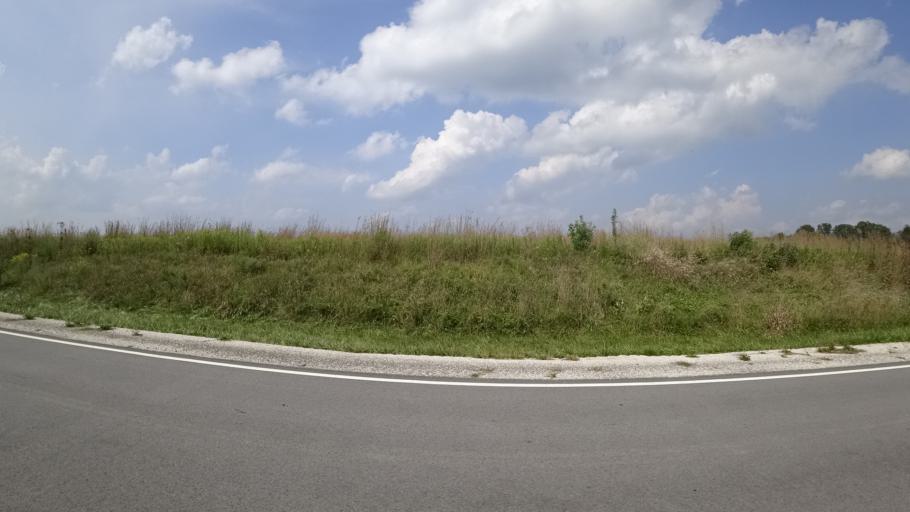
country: US
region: Illinois
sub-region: Will County
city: Goodings Grove
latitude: 41.6659
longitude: -87.9053
